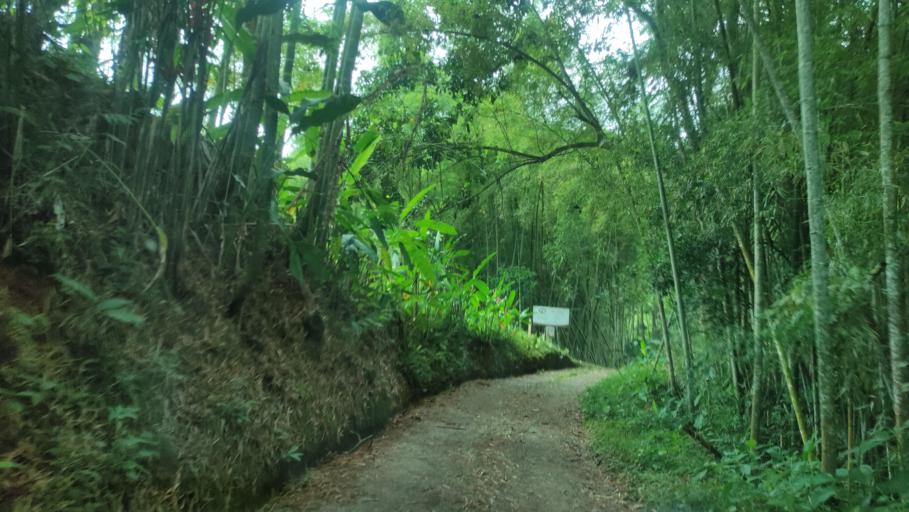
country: CO
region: Caldas
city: Palestina
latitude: 5.0669
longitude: -75.5917
